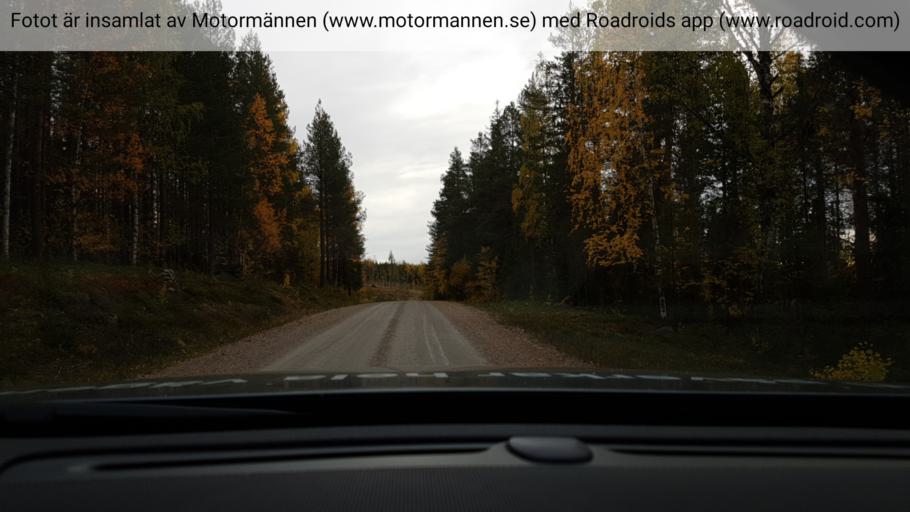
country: SE
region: Norrbotten
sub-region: Overkalix Kommun
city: OEverkalix
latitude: 66.2851
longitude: 22.9737
